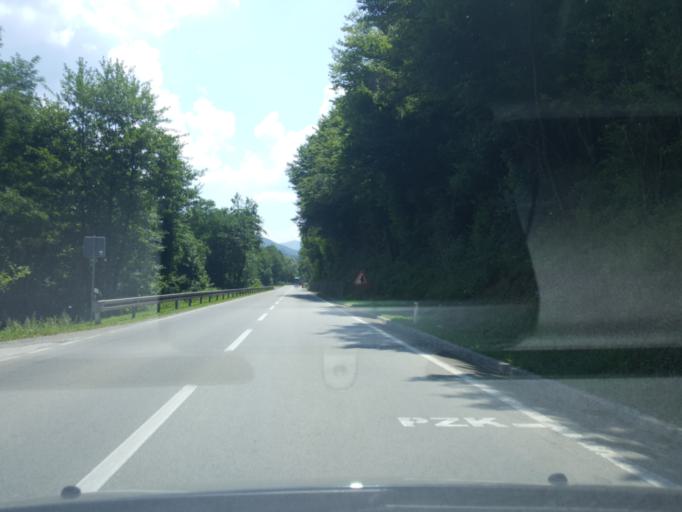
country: RS
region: Central Serbia
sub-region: Moravicki Okrug
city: Gornji Milanovac
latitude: 44.0806
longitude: 20.4835
